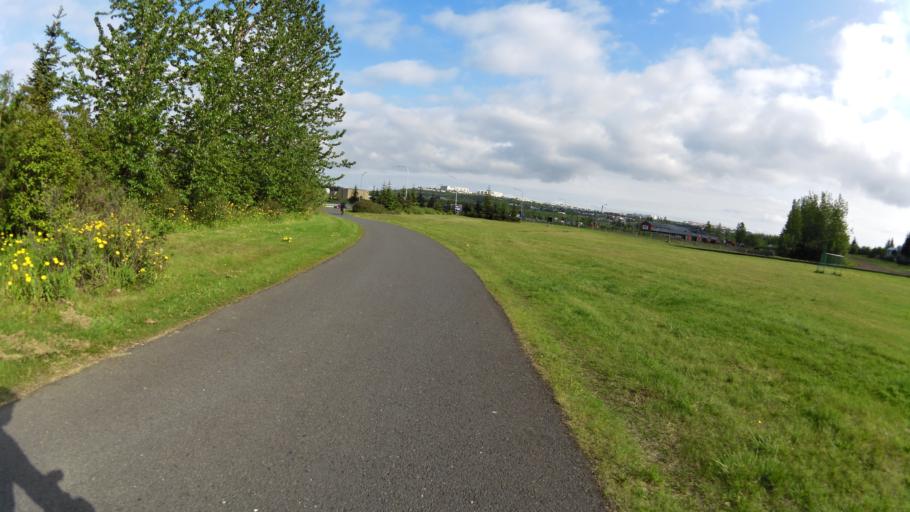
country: IS
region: Capital Region
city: Reykjavik
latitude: 64.1231
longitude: -21.8502
